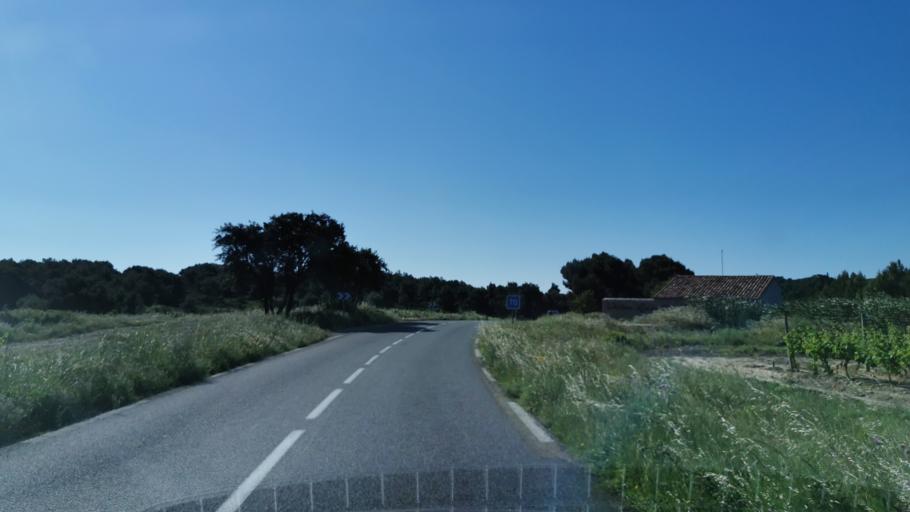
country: FR
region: Languedoc-Roussillon
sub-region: Departement de l'Aude
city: Armissan
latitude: 43.1590
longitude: 3.1504
